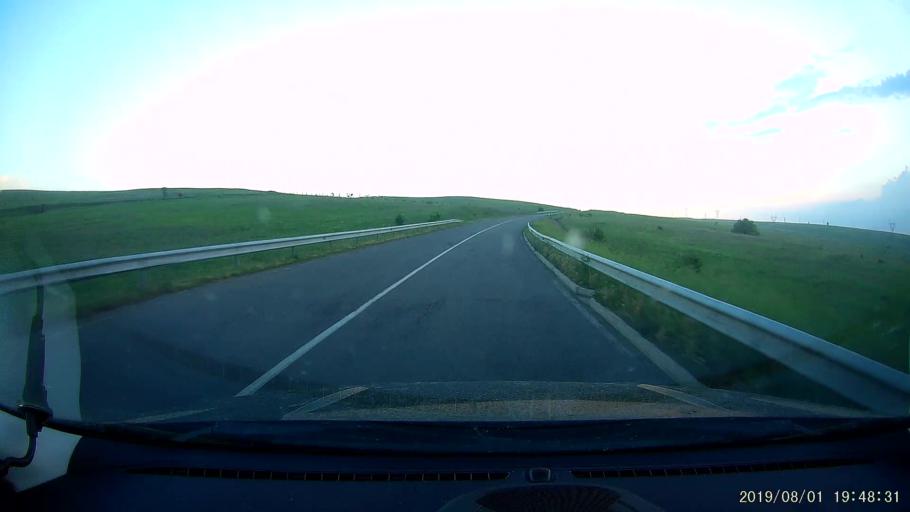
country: BG
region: Burgas
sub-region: Obshtina Karnobat
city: Karnobat
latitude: 42.6356
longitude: 26.9486
